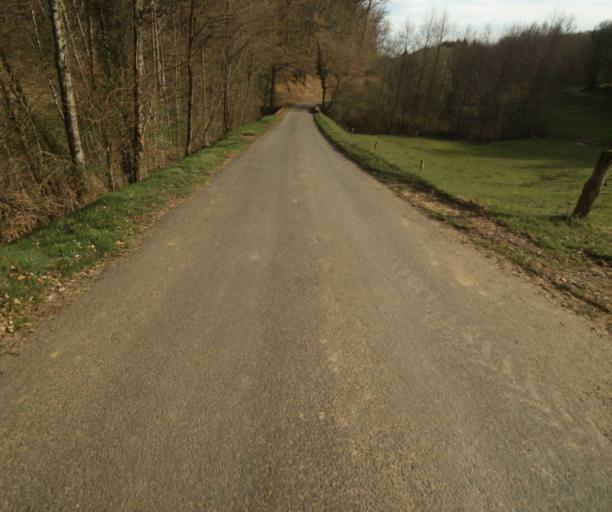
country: FR
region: Limousin
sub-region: Departement de la Correze
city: Naves
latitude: 45.2992
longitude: 1.7548
